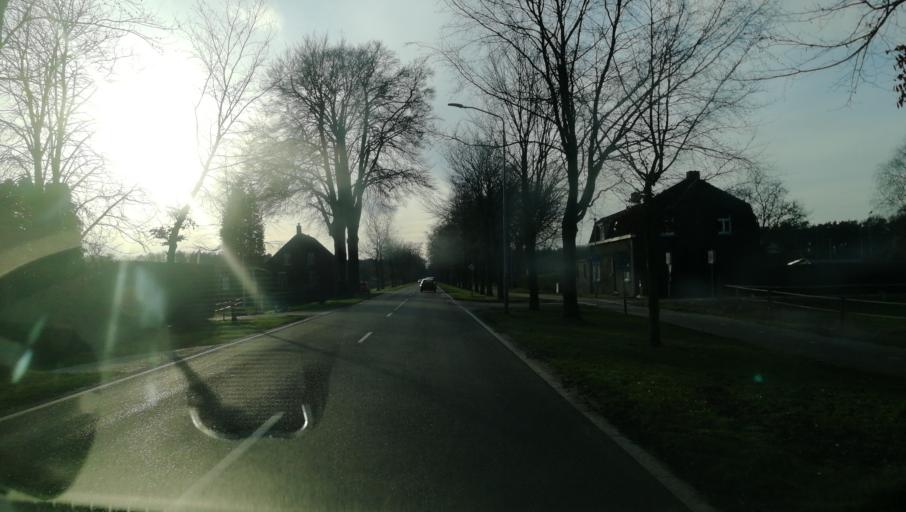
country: NL
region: Limburg
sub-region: Gemeente Venlo
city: Tegelen
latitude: 51.3539
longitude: 6.1237
